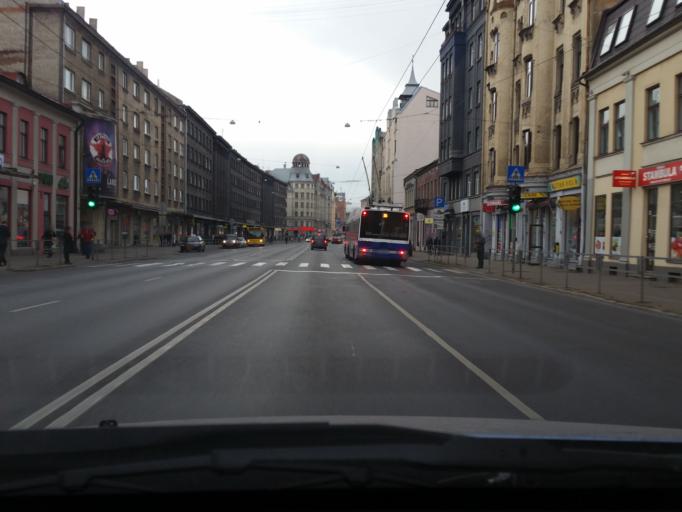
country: LV
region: Riga
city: Riga
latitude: 56.9610
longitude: 24.1325
